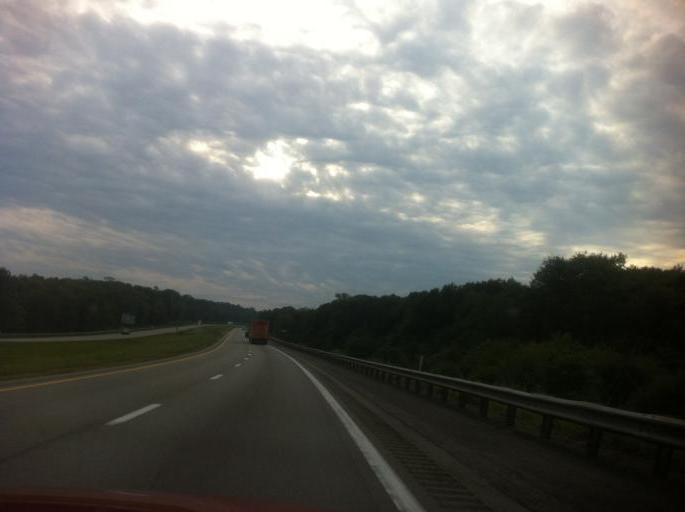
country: US
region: Pennsylvania
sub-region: Mercer County
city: Grove City
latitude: 41.1963
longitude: -79.8840
